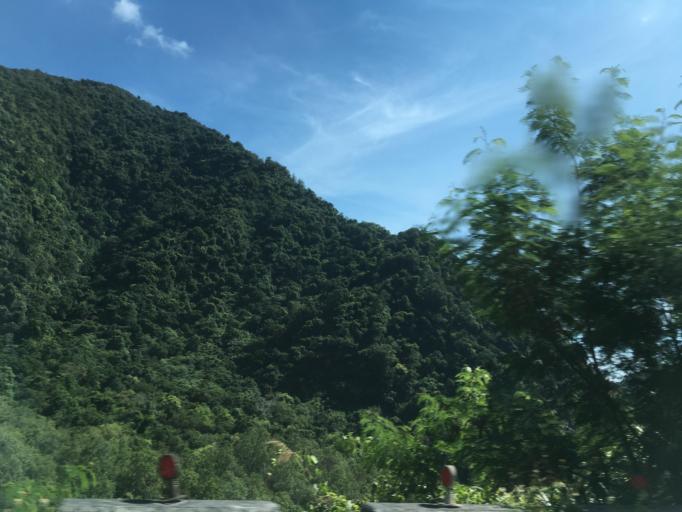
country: TW
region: Taiwan
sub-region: Yilan
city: Yilan
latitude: 24.4201
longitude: 121.7295
